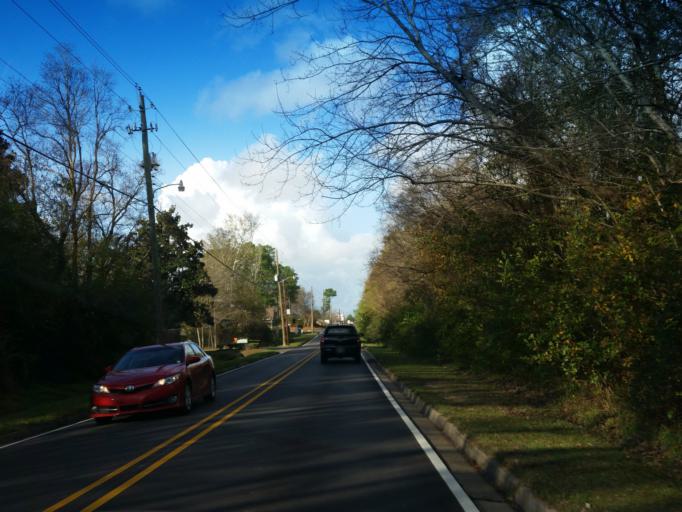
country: US
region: Mississippi
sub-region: Lamar County
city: West Hattiesburg
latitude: 31.3154
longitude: -89.3480
